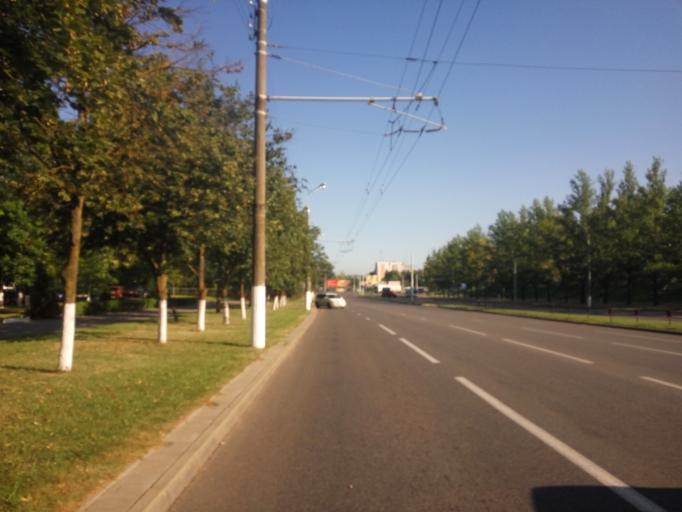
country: BY
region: Vitebsk
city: Vitebsk
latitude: 55.1935
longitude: 30.2495
